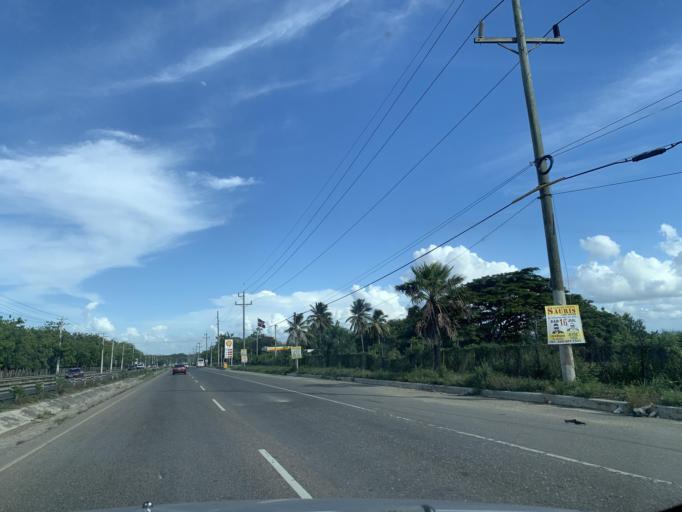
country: DO
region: Santiago
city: Villa Gonzalez
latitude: 19.5303
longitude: -70.7773
